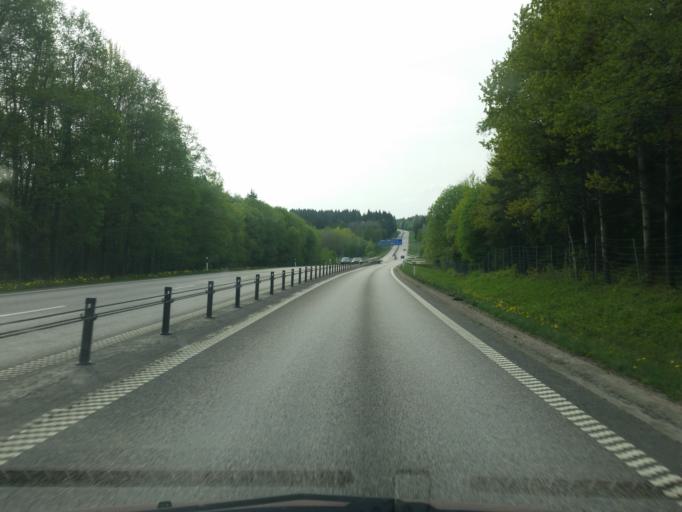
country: SE
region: Vaestra Goetaland
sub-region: Ulricehamns Kommun
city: Ulricehamn
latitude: 57.7962
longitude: 13.5430
